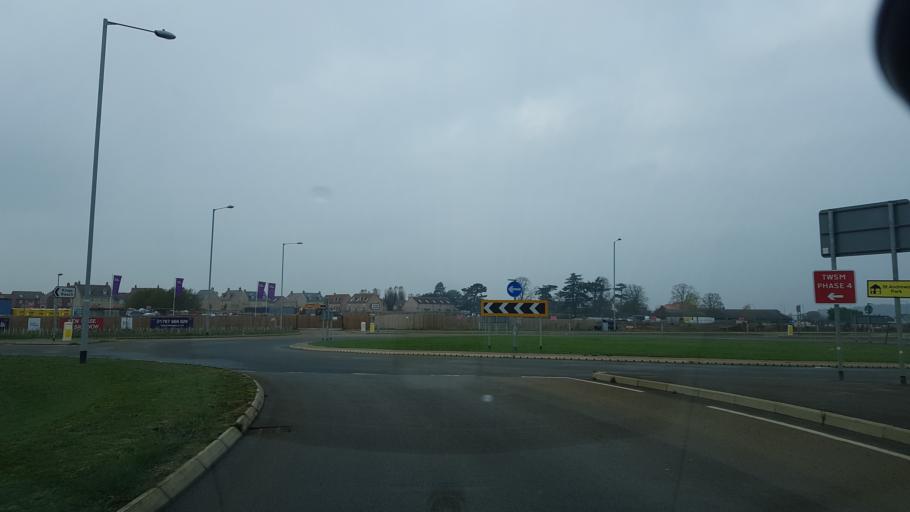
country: GB
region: England
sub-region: Central Bedfordshire
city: Biggleswade
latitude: 52.0976
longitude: -0.2425
